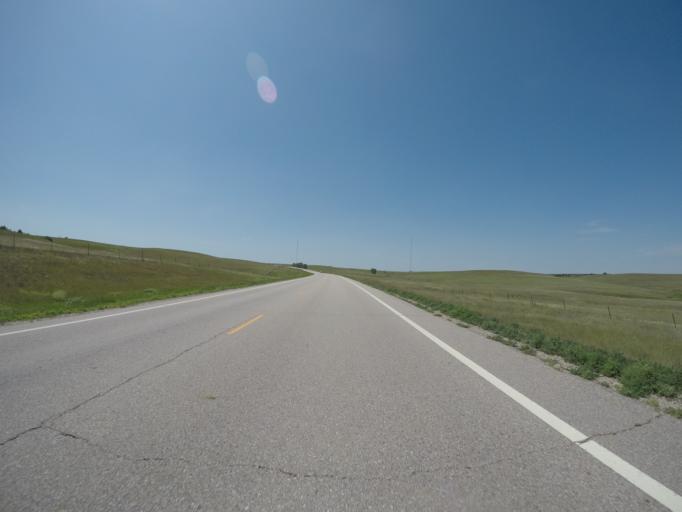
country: US
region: Kansas
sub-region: Osborne County
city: Osborne
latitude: 39.4906
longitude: -98.6965
